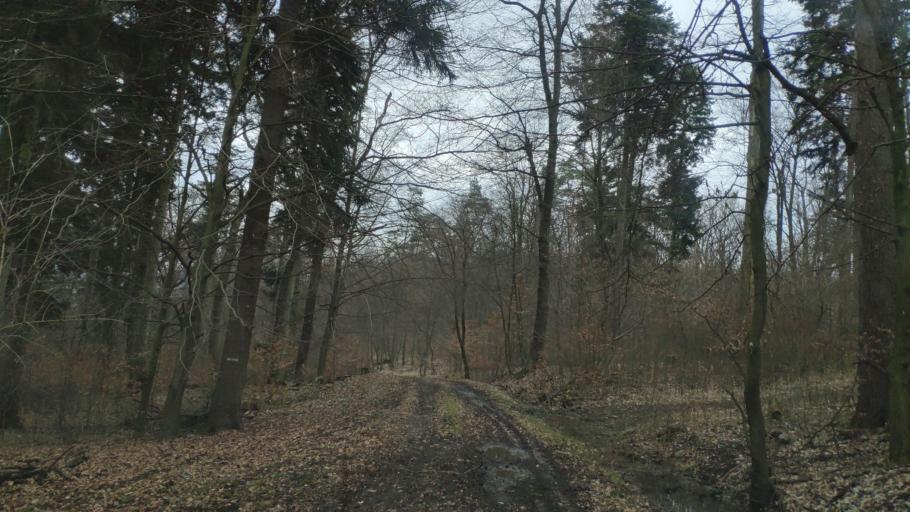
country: SK
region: Presovsky
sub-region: Okres Presov
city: Presov
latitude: 49.0720
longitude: 21.2792
